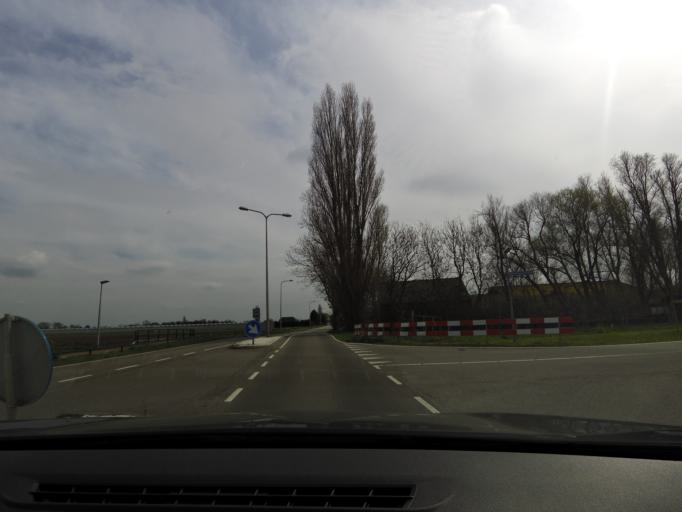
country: NL
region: South Holland
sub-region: Gemeente Albrandswaard
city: Rhoon
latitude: 51.8511
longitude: 4.4093
